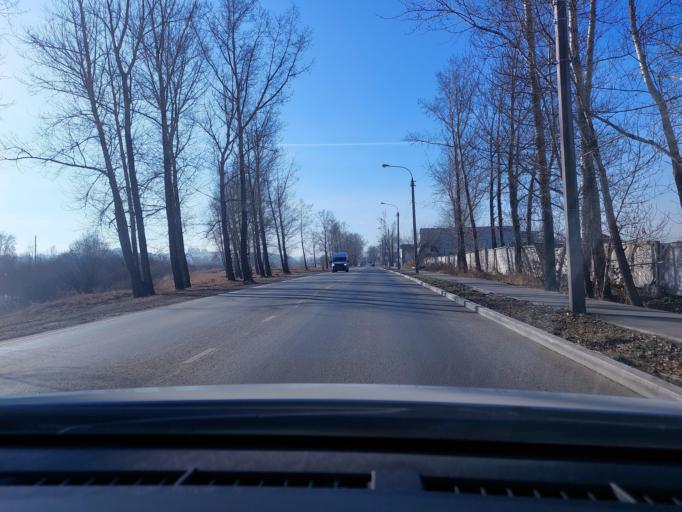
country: RU
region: Irkutsk
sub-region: Irkutskiy Rayon
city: Irkutsk
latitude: 52.3087
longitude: 104.2595
